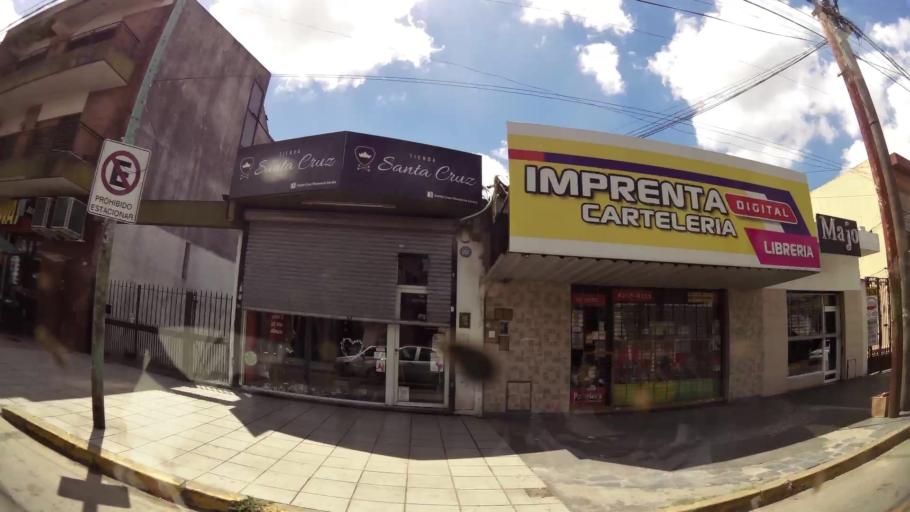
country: AR
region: Buenos Aires
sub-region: Partido de Quilmes
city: Quilmes
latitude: -34.8088
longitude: -58.2742
